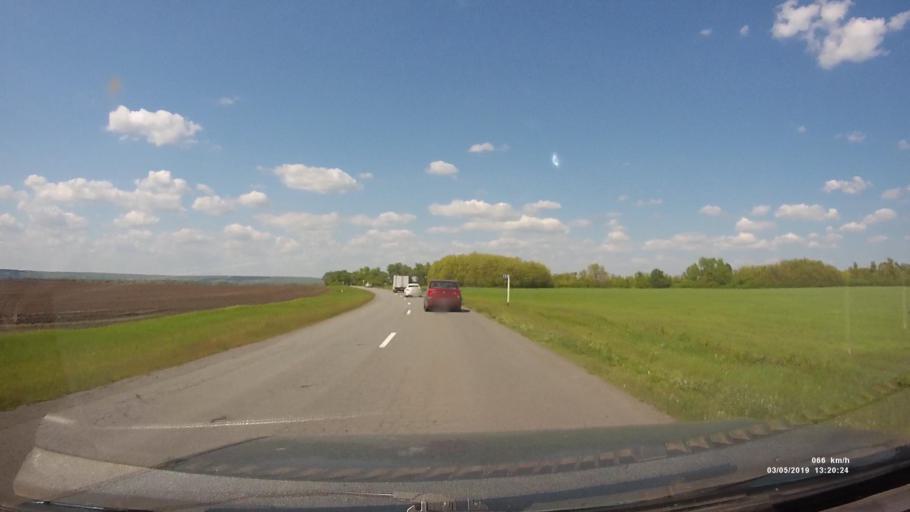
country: RU
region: Rostov
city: Semikarakorsk
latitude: 47.5460
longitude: 40.7538
